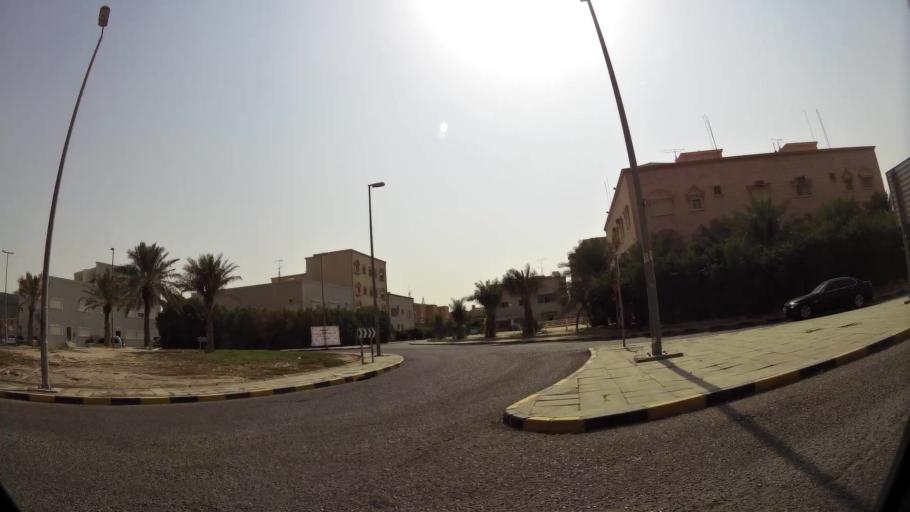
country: KW
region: Muhafazat al Jahra'
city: Al Jahra'
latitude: 29.3243
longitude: 47.6625
